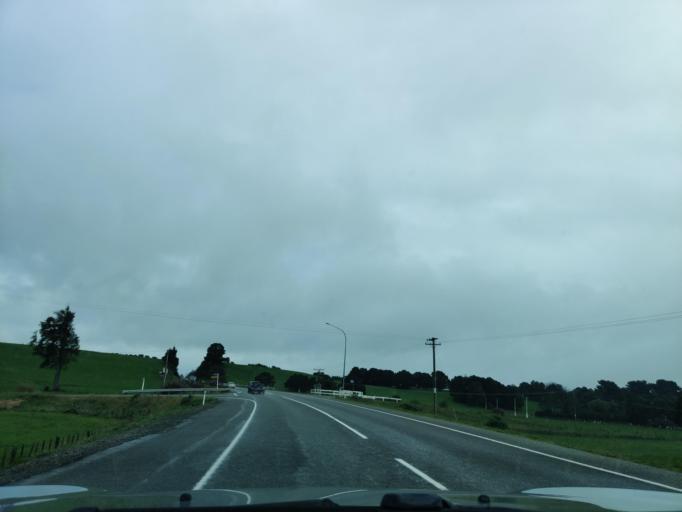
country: NZ
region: Manawatu-Wanganui
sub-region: Palmerston North City
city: Palmerston North
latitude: -40.0560
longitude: 176.2301
